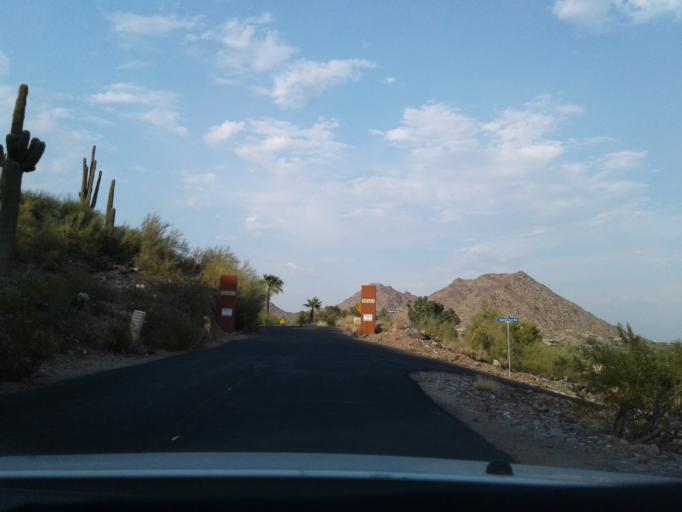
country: US
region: Arizona
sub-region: Maricopa County
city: Paradise Valley
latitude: 33.5404
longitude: -111.9851
